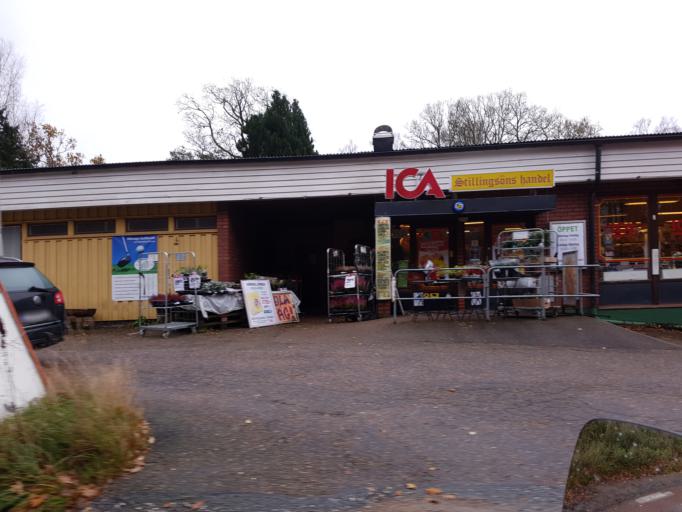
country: SE
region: Vaestra Goetaland
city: Svanesund
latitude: 58.1930
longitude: 11.8296
